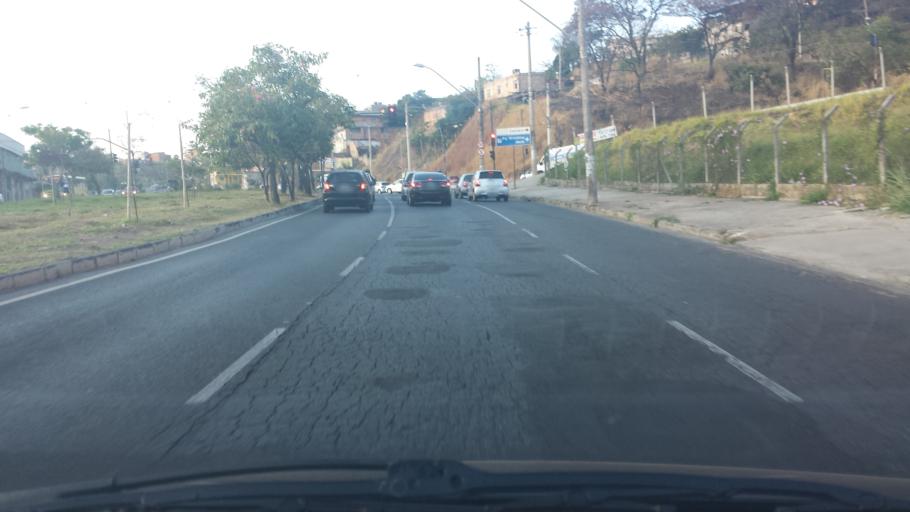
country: BR
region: Minas Gerais
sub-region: Belo Horizonte
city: Belo Horizonte
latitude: -19.8931
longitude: -43.9934
